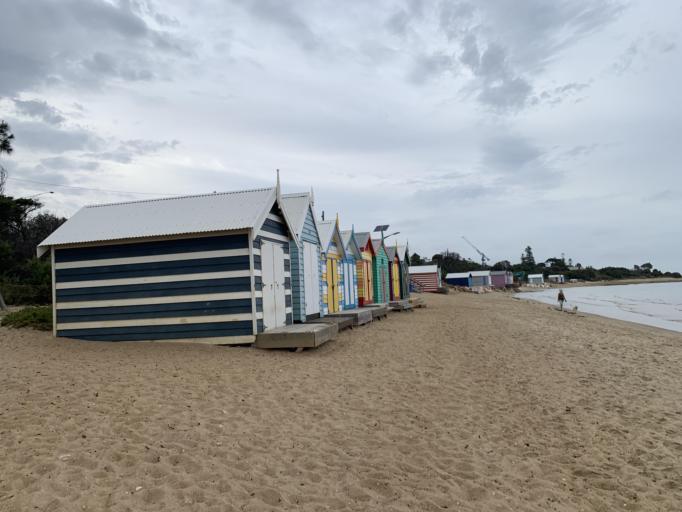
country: AU
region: Victoria
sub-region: Bayside
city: North Brighton
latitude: -37.9197
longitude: 144.9874
